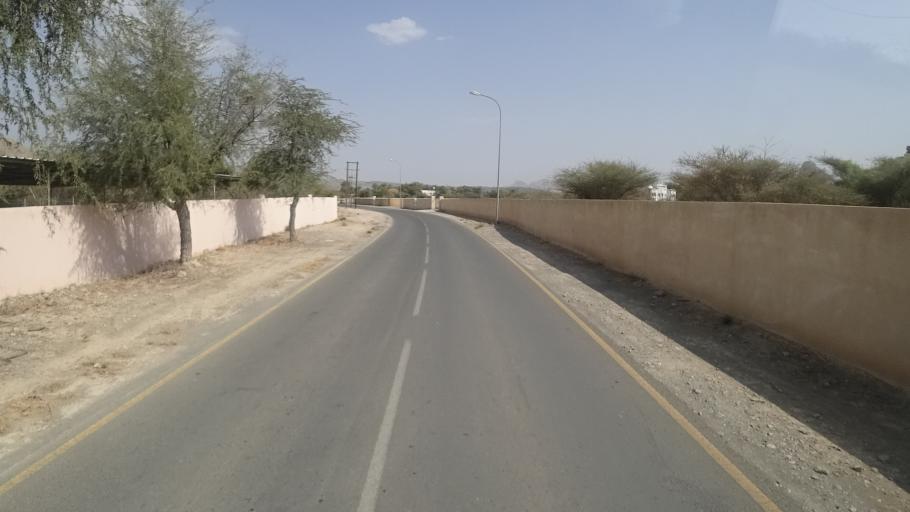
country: OM
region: Muhafazat ad Dakhiliyah
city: Bahla'
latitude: 23.1071
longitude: 57.2966
